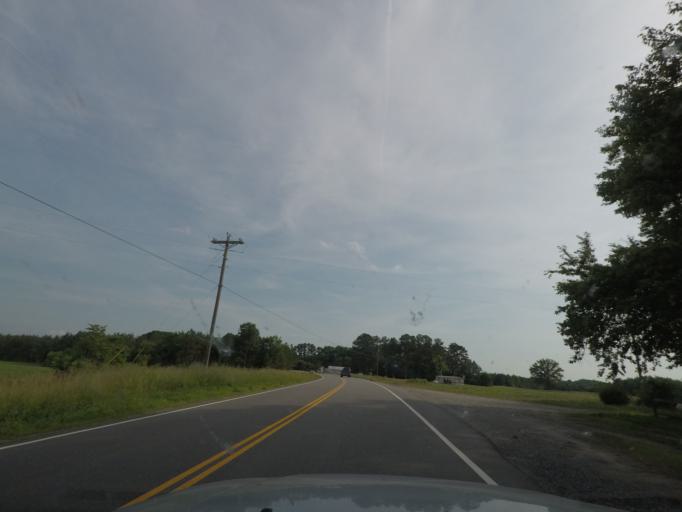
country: US
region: Virginia
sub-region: Mecklenburg County
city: Chase City
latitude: 36.8480
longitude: -78.5952
